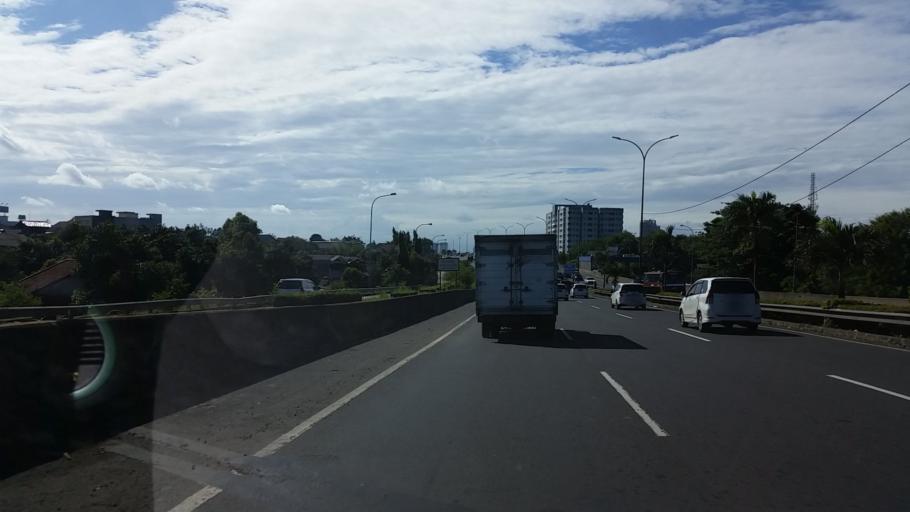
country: ID
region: Banten
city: South Tangerang
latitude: -6.2578
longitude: 106.7656
